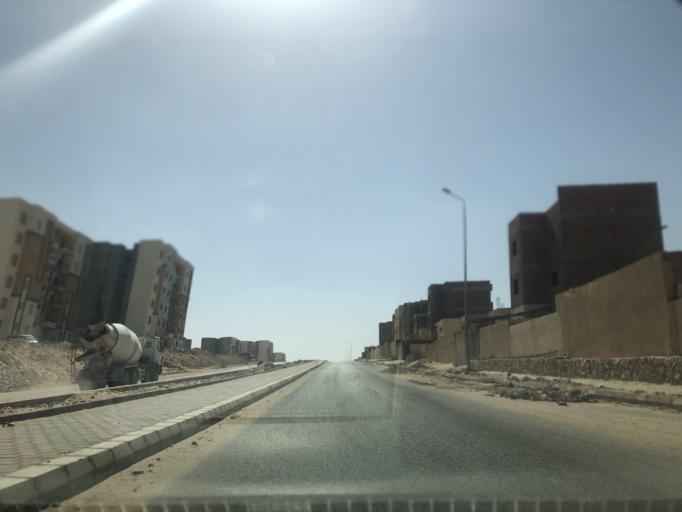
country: EG
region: Al Jizah
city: Madinat Sittah Uktubar
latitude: 29.9284
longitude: 31.0048
